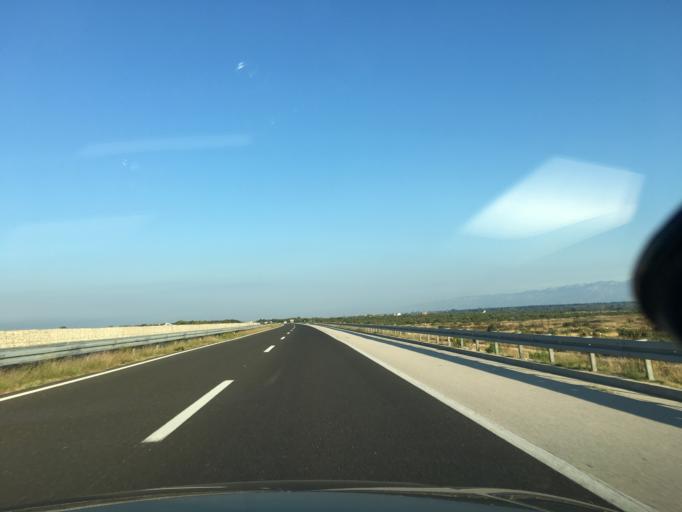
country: HR
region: Zadarska
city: Polaca
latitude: 44.0798
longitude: 15.5091
